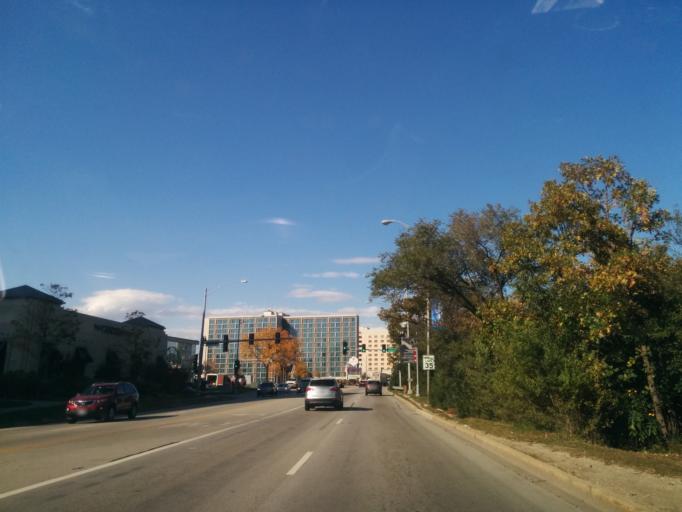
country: US
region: Illinois
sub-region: Cook County
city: Schiller Park
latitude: 41.9744
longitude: -87.8625
